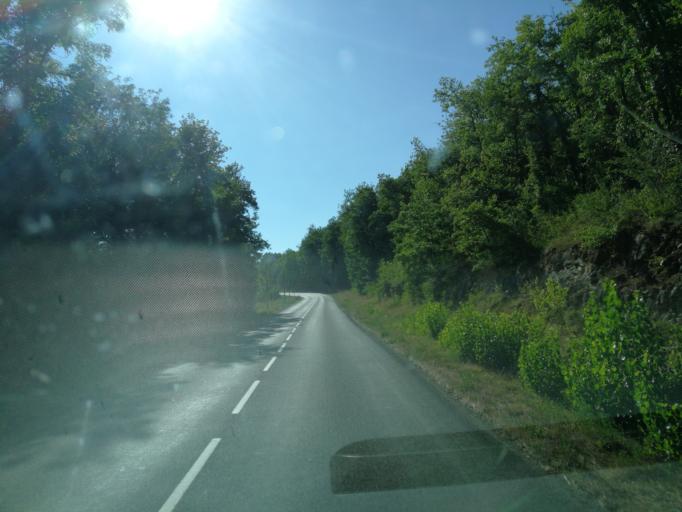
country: FR
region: Midi-Pyrenees
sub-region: Departement du Lot
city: Gourdon
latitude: 44.7104
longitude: 1.3268
